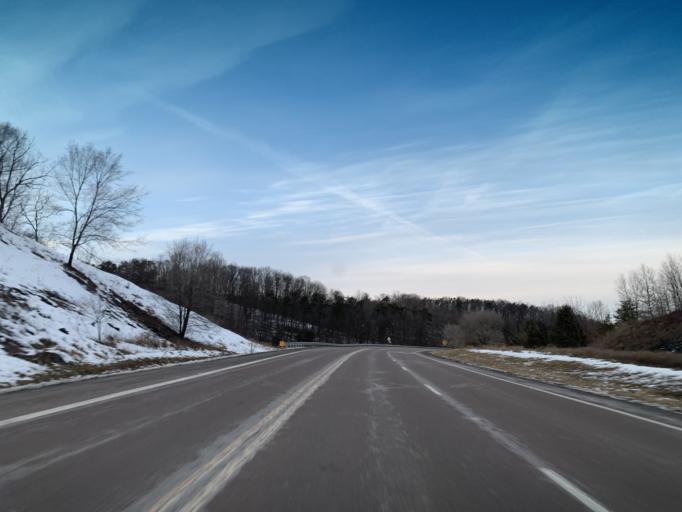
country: US
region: Maryland
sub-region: Allegany County
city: Cumberland
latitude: 39.6894
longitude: -78.7148
